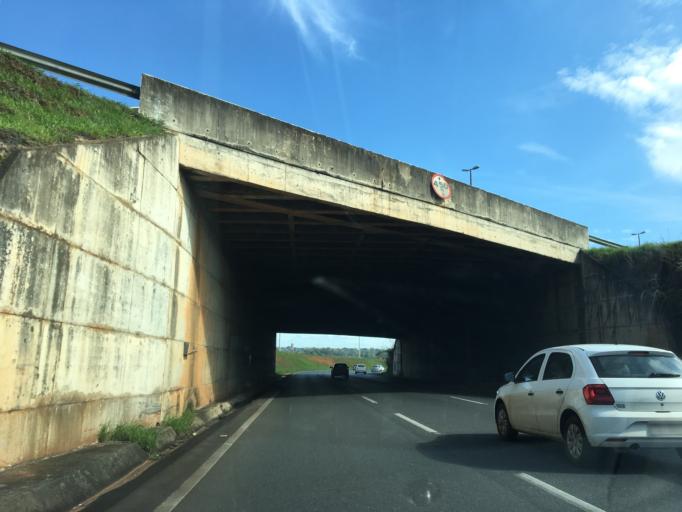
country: BR
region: Federal District
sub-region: Brasilia
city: Brasilia
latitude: -15.8637
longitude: -47.9385
